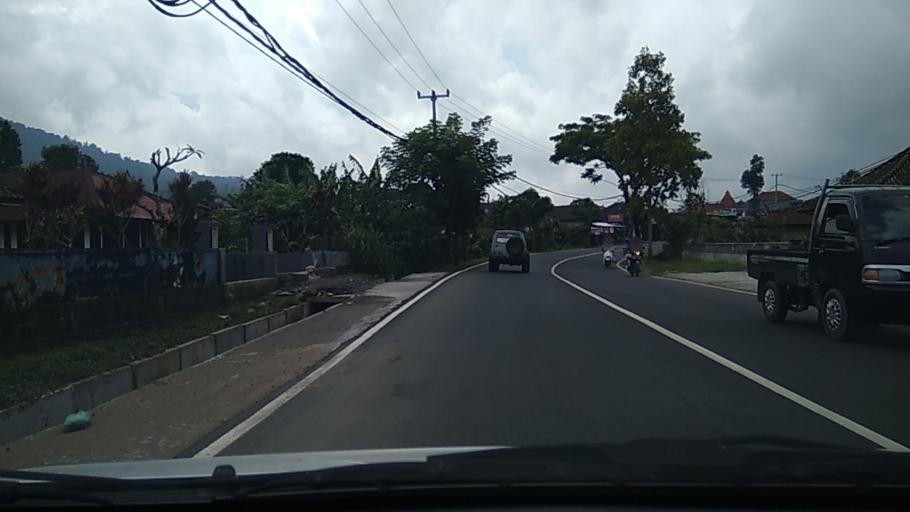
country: ID
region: Bali
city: Munduk
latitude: -8.2536
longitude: 115.1570
